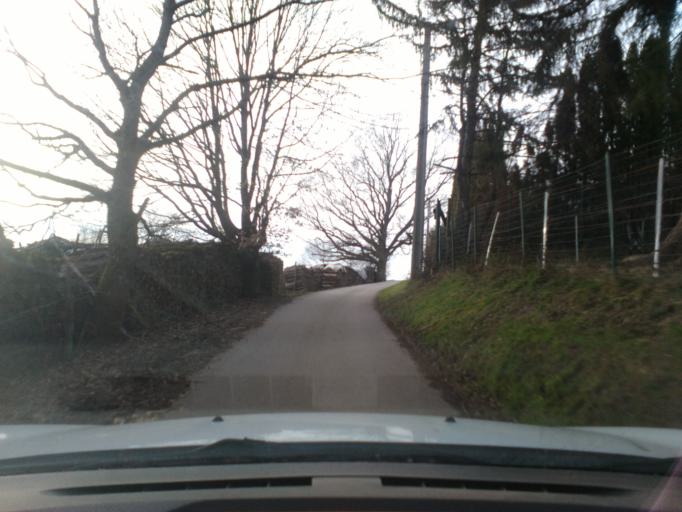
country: FR
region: Lorraine
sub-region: Departement des Vosges
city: Jeanmenil
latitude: 48.3283
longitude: 6.7135
